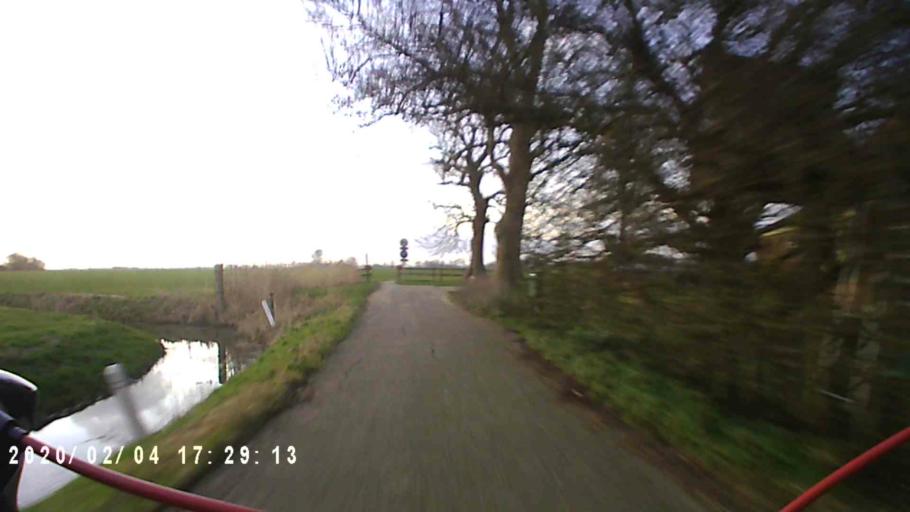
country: NL
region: Groningen
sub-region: Gemeente Zuidhorn
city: Aduard
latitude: 53.2719
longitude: 6.5045
